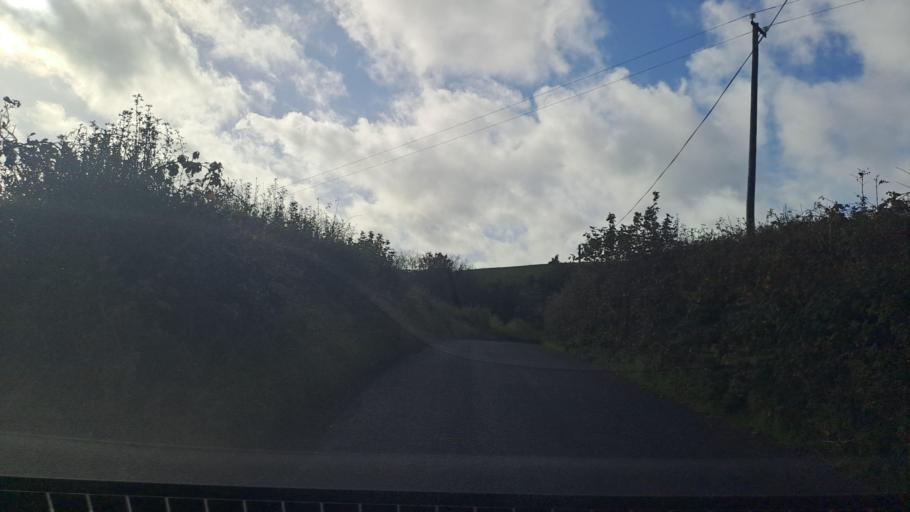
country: IE
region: Ulster
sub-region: An Cabhan
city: Cootehill
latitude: 54.0339
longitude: -7.0056
